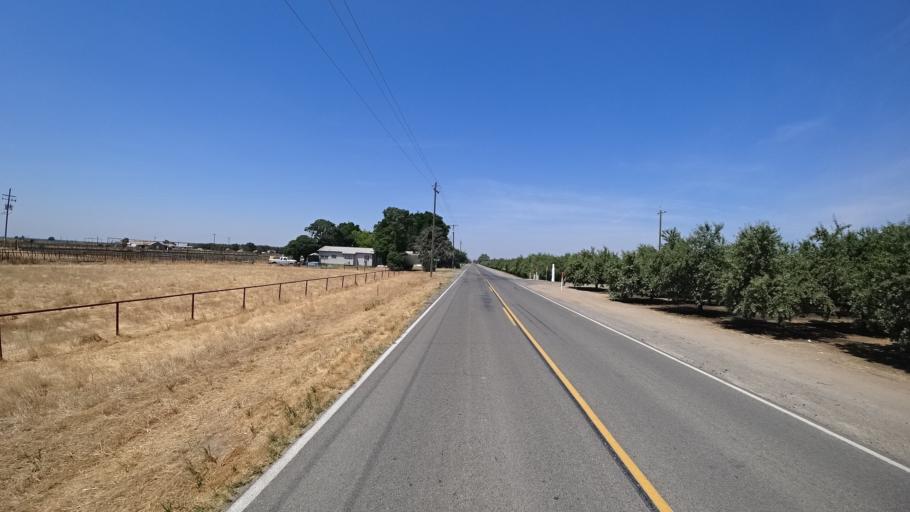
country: US
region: California
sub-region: Kings County
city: Lucerne
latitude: 36.4013
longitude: -119.6005
